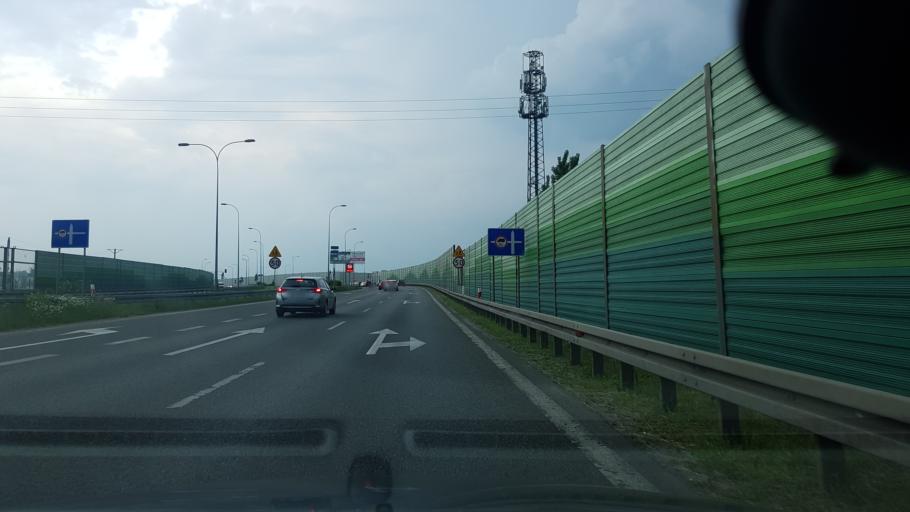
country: PL
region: Masovian Voivodeship
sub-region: Powiat legionowski
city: Jablonna
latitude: 52.3716
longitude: 20.9339
